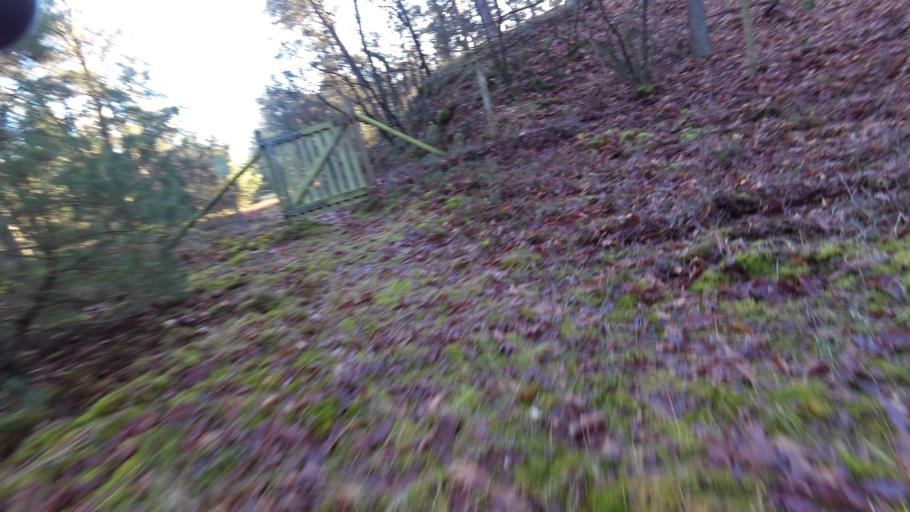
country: NL
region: Gelderland
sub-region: Gemeente Barneveld
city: Garderen
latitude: 52.2101
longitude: 5.7178
